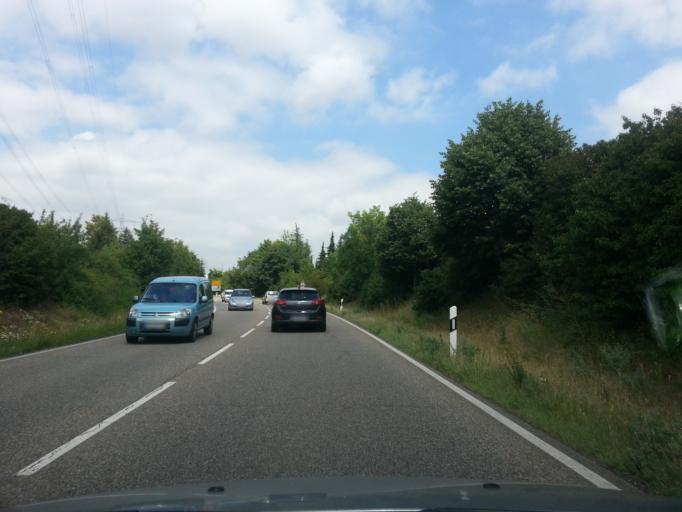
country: DE
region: Baden-Wuerttemberg
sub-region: Karlsruhe Region
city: Bruhl
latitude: 49.4108
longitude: 8.5459
